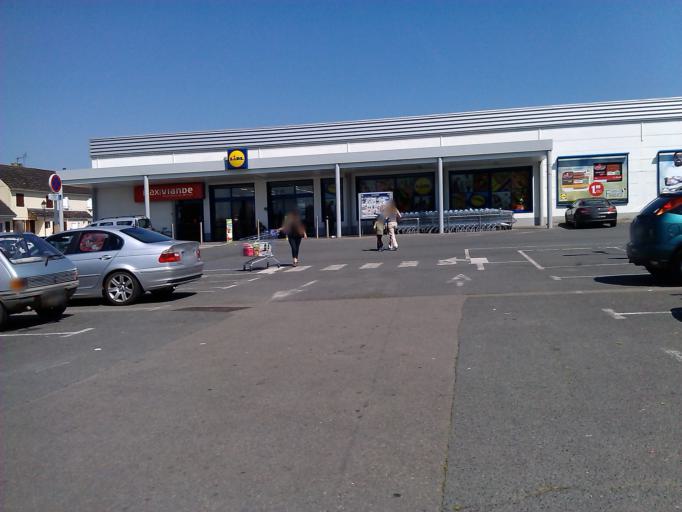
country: FR
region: Centre
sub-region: Departement de l'Indre
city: Argenton-sur-Creuse
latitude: 46.5904
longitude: 1.5293
